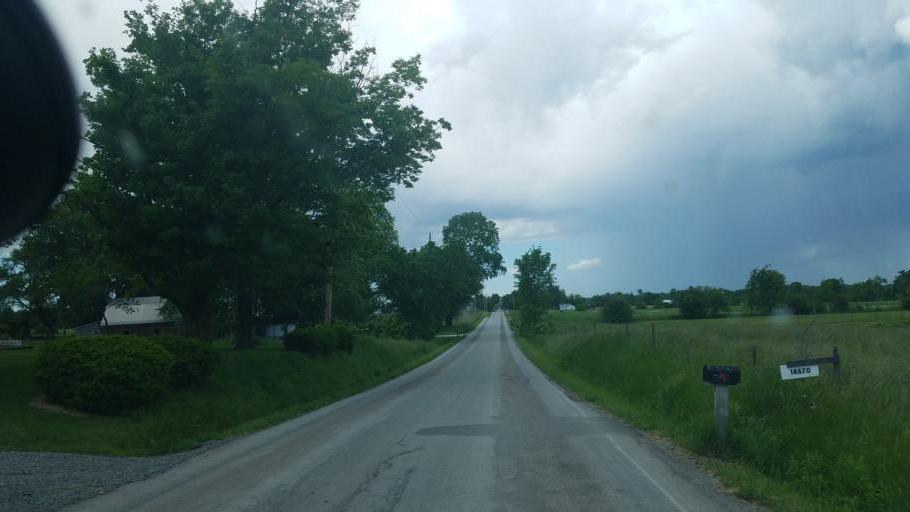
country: US
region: Ohio
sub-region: Geauga County
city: Middlefield
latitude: 41.4689
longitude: -81.0032
